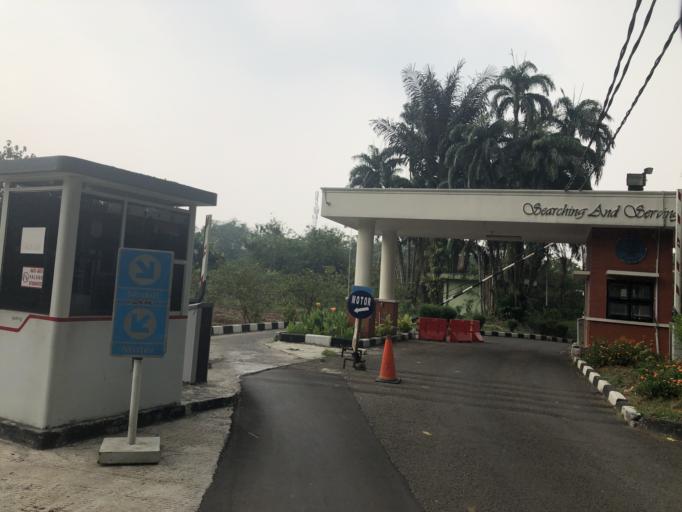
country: ID
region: West Java
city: Ciampea
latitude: -6.5518
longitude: 106.7269
